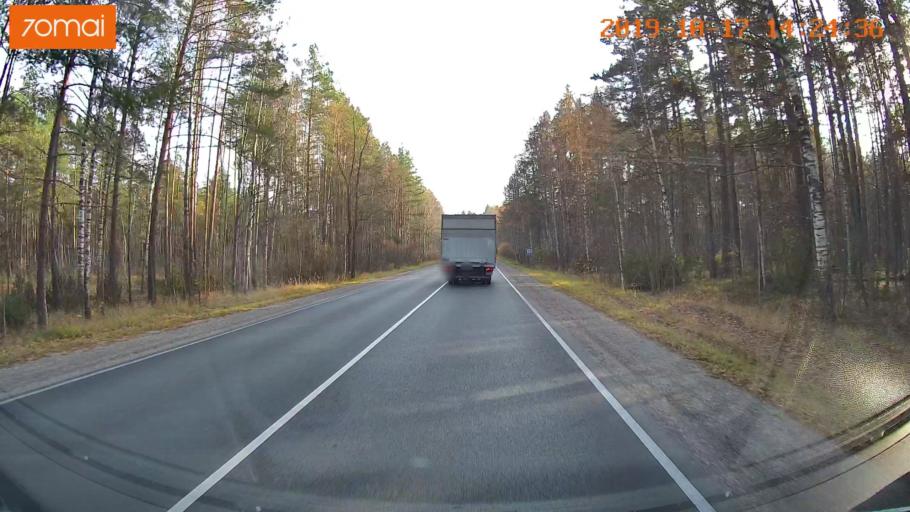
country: RU
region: Moskovskaya
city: Radovitskiy
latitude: 55.0080
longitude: 39.9698
